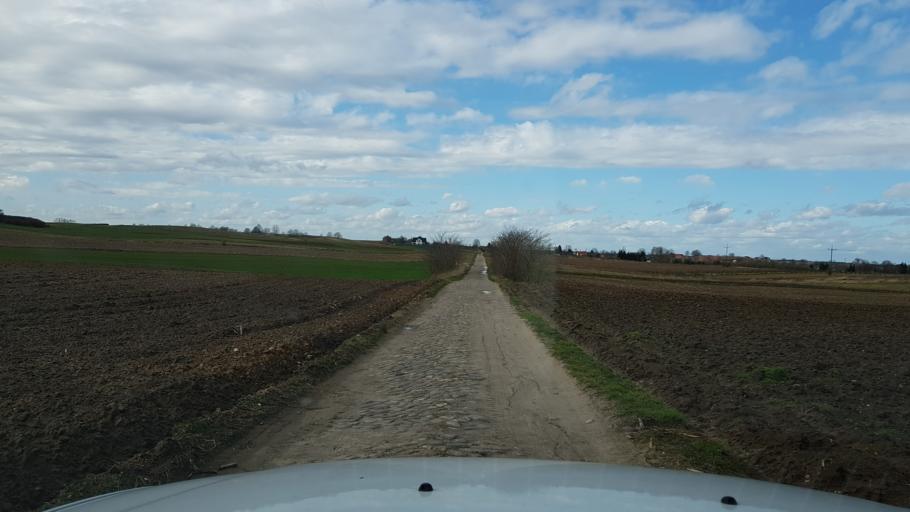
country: PL
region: West Pomeranian Voivodeship
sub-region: Powiat mysliborski
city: Barlinek
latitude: 52.9734
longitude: 15.1826
